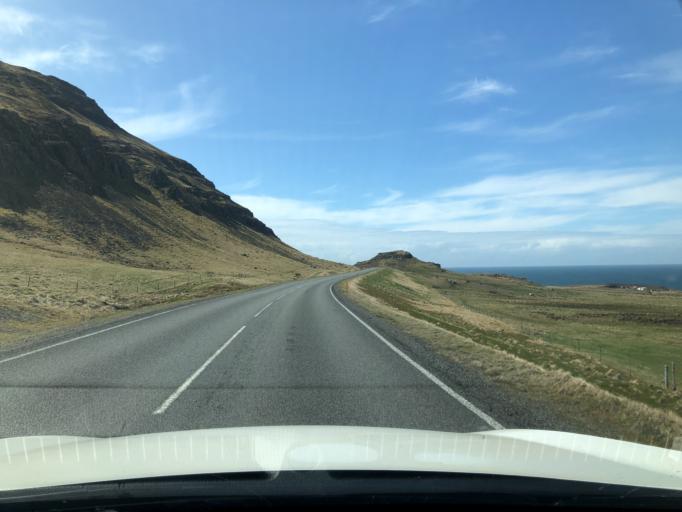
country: IS
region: Capital Region
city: Mosfellsbaer
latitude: 64.2854
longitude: -21.8170
